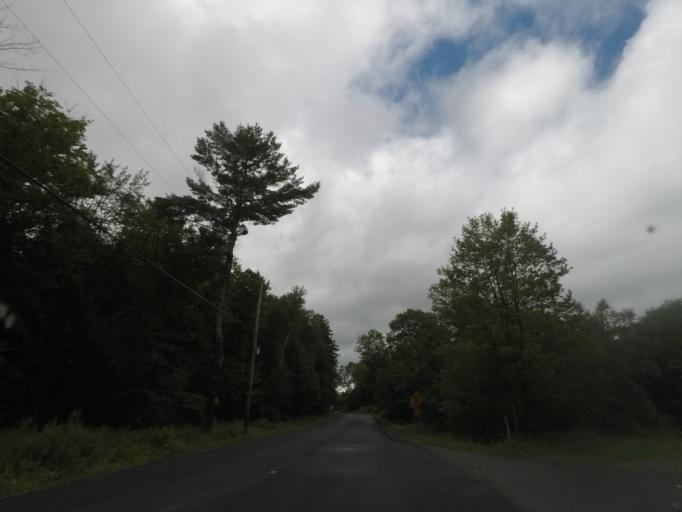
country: US
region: New York
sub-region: Rensselaer County
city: Poestenkill
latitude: 42.6907
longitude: -73.4646
